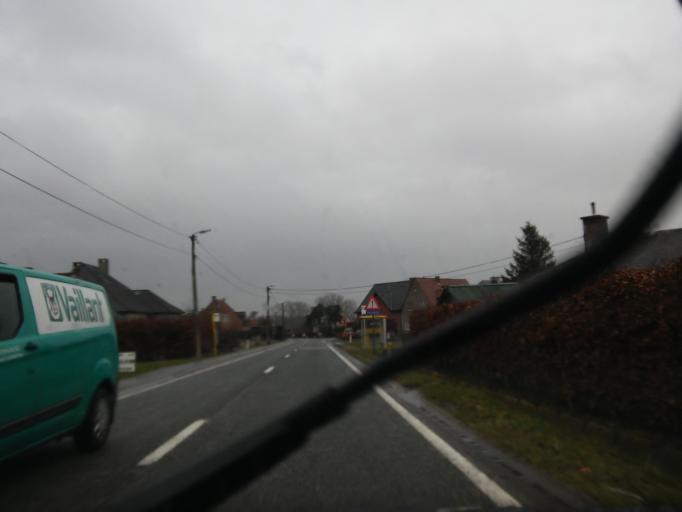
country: BE
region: Flanders
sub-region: Provincie Vlaams-Brabant
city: Gooik
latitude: 50.7589
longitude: 4.1026
